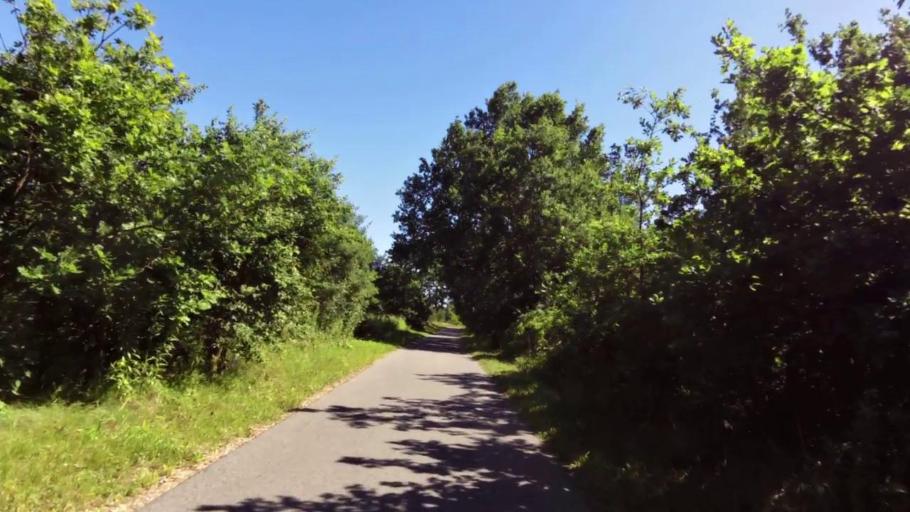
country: PL
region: West Pomeranian Voivodeship
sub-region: Powiat bialogardzki
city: Karlino
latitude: 54.0472
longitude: 15.8804
